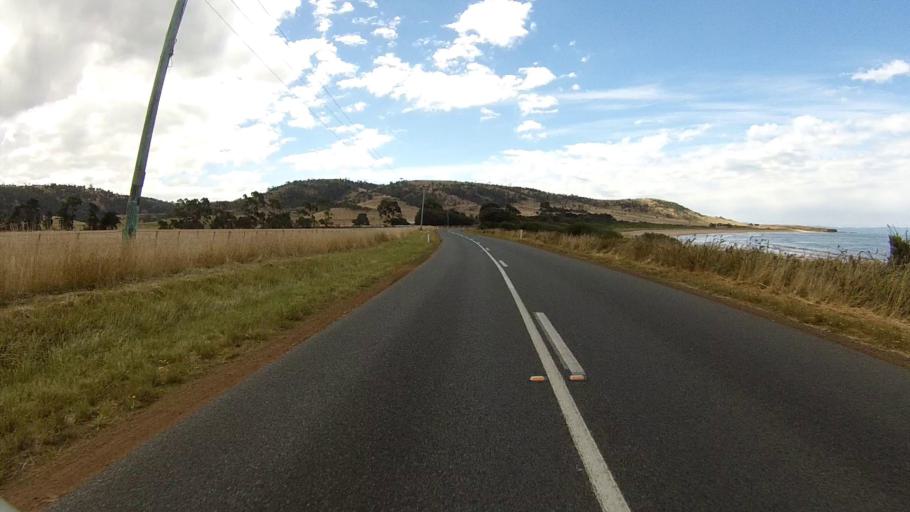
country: AU
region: Tasmania
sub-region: Sorell
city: Sorell
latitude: -42.2045
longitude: 148.0426
